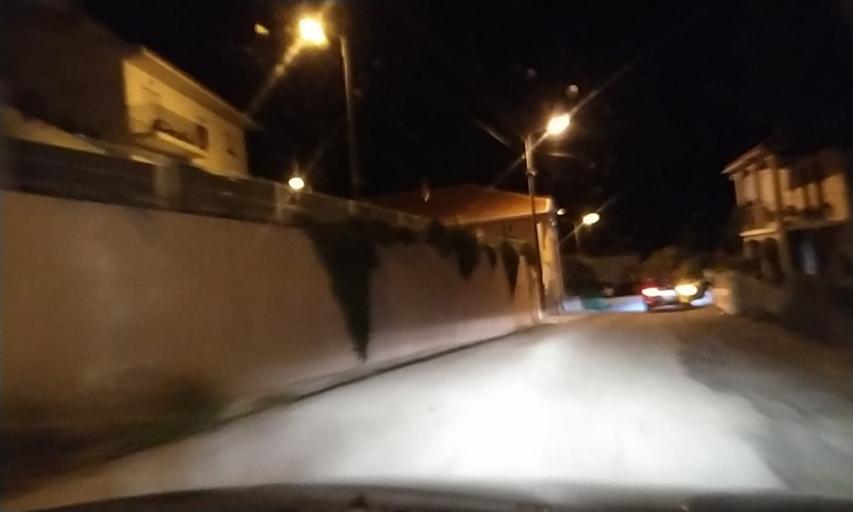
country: PT
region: Vila Real
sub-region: Santa Marta de Penaguiao
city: Santa Marta de Penaguiao
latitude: 41.1973
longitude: -7.8251
